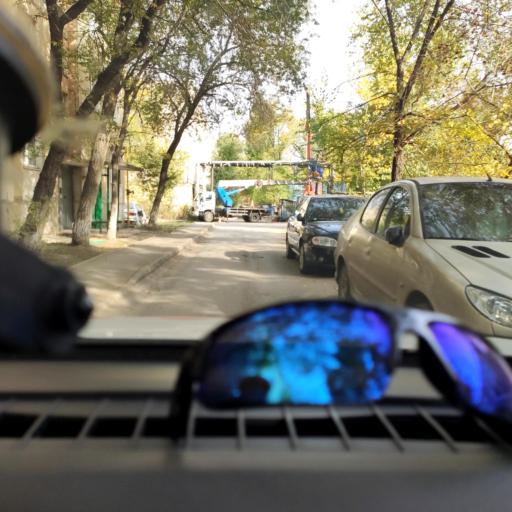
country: RU
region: Samara
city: Samara
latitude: 53.1210
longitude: 50.0908
